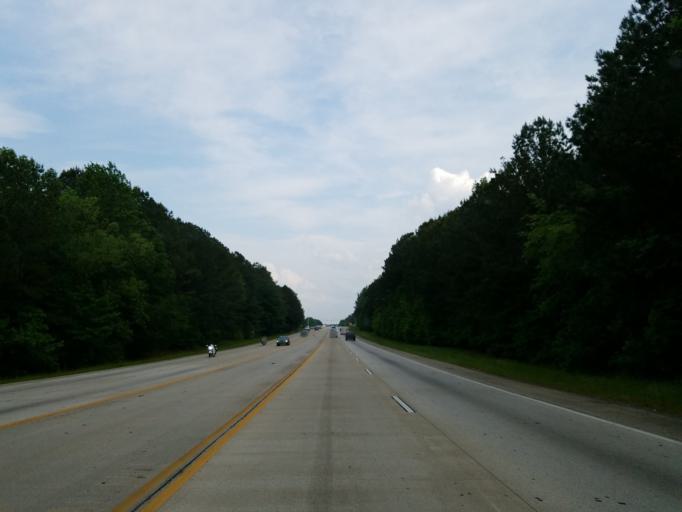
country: US
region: Georgia
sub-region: Cobb County
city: Powder Springs
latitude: 33.8454
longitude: -84.6906
